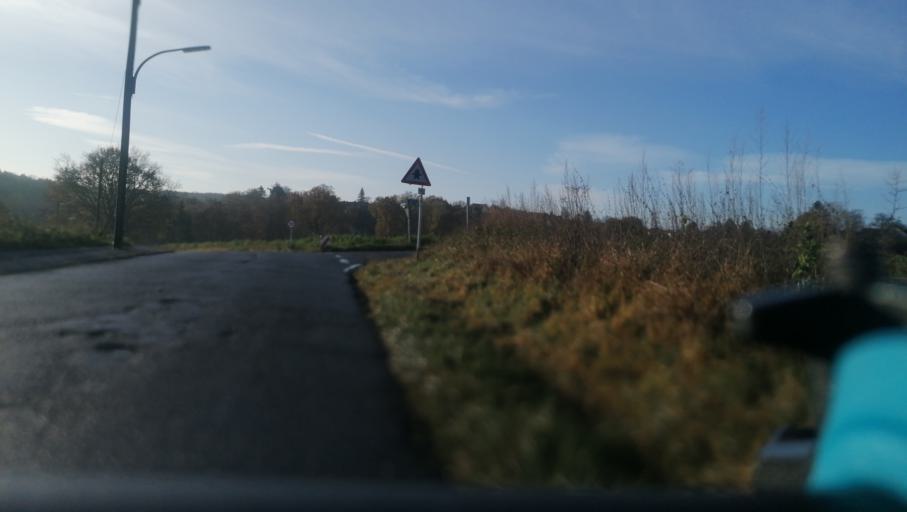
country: DE
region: North Rhine-Westphalia
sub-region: Regierungsbezirk Arnsberg
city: Dortmund
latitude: 51.4599
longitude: 7.4949
